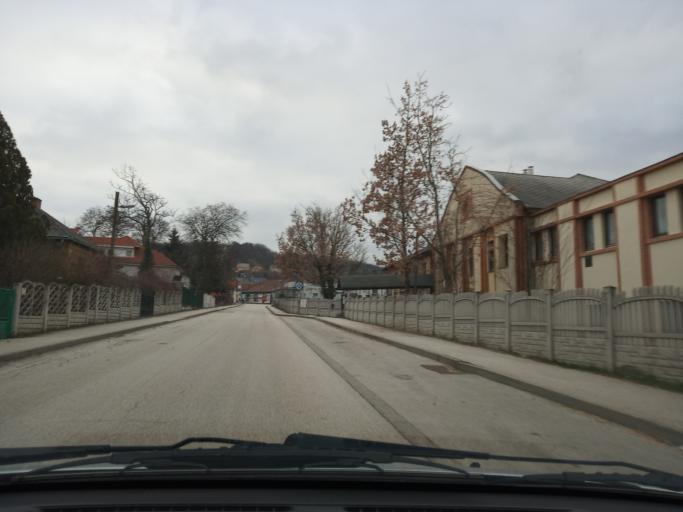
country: HU
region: Komarom-Esztergom
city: Dorog
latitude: 47.7220
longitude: 18.7308
